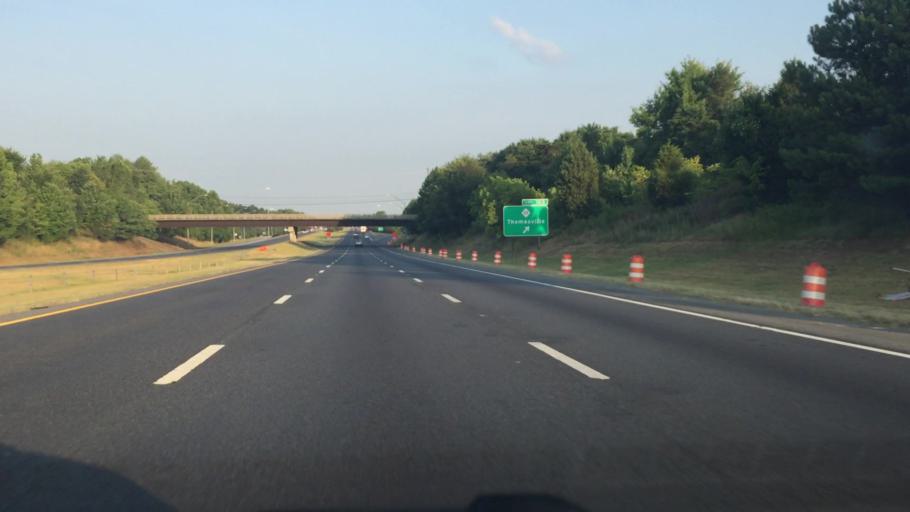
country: US
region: North Carolina
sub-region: Davidson County
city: Thomasville
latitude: 35.8596
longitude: -80.0647
